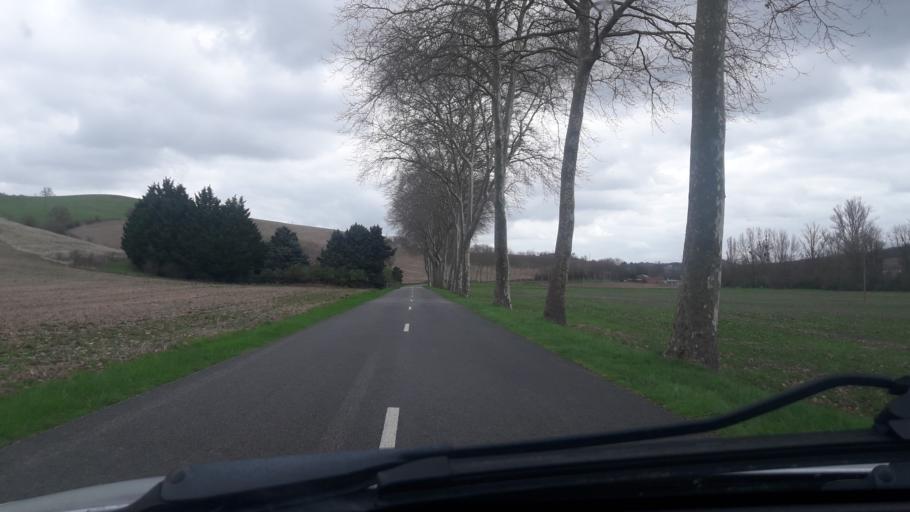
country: FR
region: Midi-Pyrenees
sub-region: Departement de la Haute-Garonne
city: Montesquieu-Volvestre
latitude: 43.2446
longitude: 1.2612
